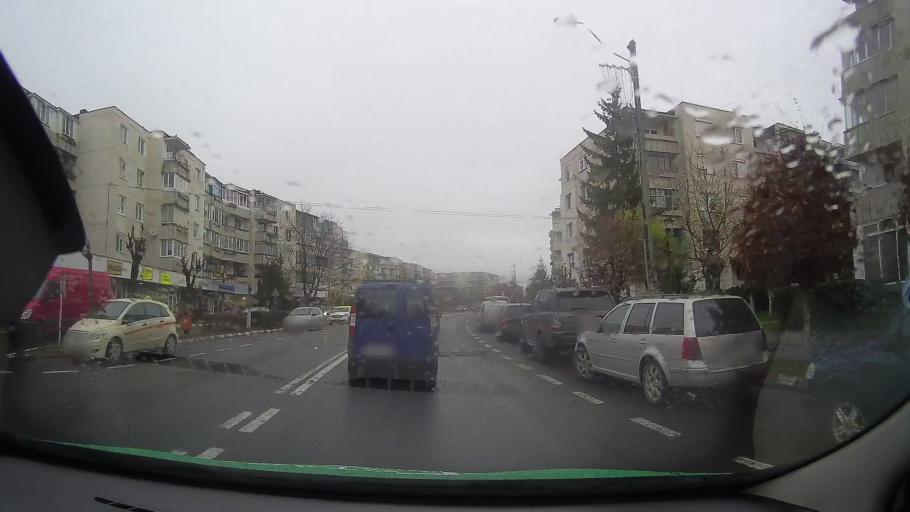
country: RO
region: Mures
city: Reghin-Sat
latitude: 46.7824
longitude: 24.7090
